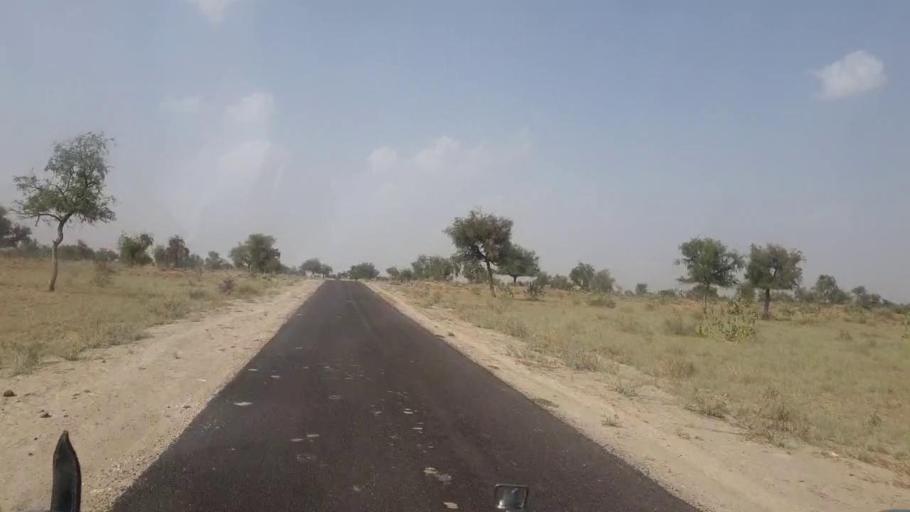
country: PK
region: Sindh
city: Islamkot
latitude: 25.1721
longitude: 70.2885
